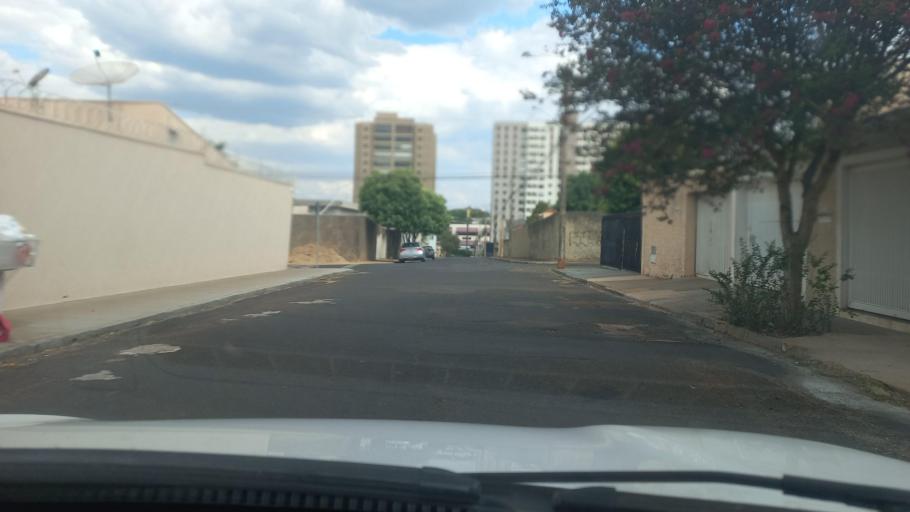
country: BR
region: Minas Gerais
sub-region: Uberaba
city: Uberaba
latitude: -19.7647
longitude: -47.9544
